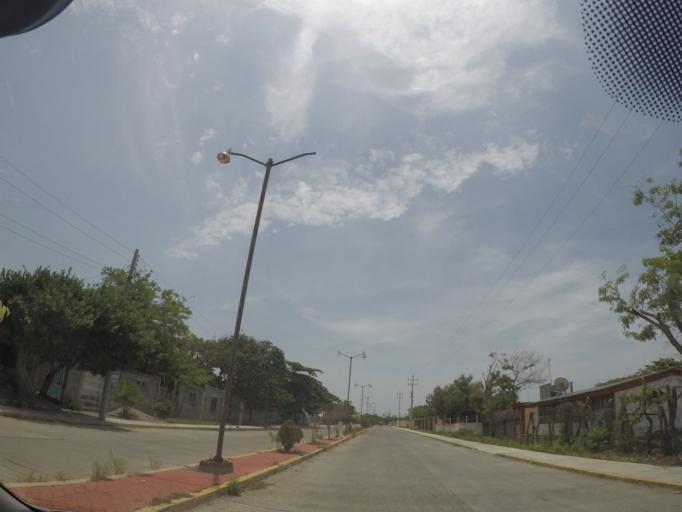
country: MX
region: Oaxaca
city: San Mateo del Mar
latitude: 16.2096
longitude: -94.9926
